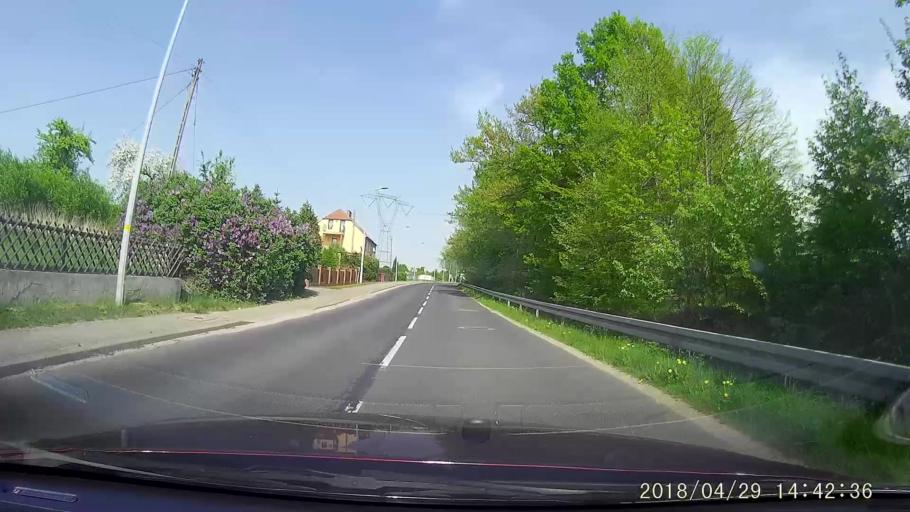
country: DE
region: Saxony
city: Ostritz
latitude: 51.0597
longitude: 14.9758
